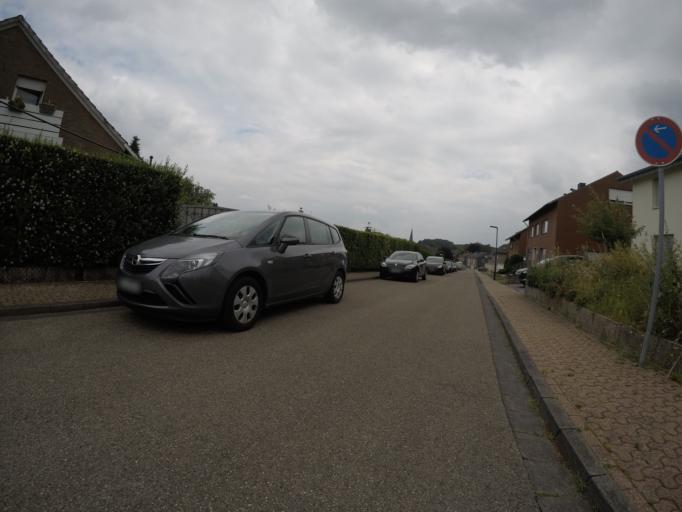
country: DE
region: North Rhine-Westphalia
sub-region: Regierungsbezirk Dusseldorf
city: Wesel
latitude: 51.7264
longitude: 6.6737
